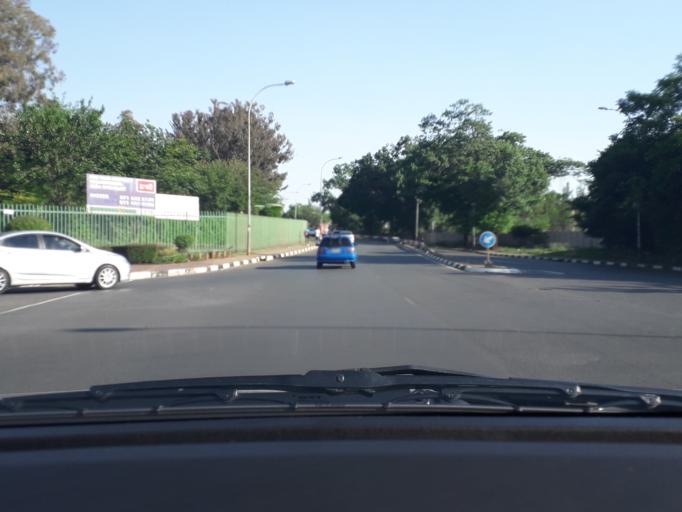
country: ZA
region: Gauteng
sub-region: City of Johannesburg Metropolitan Municipality
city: Johannesburg
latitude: -26.1819
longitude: 28.1042
